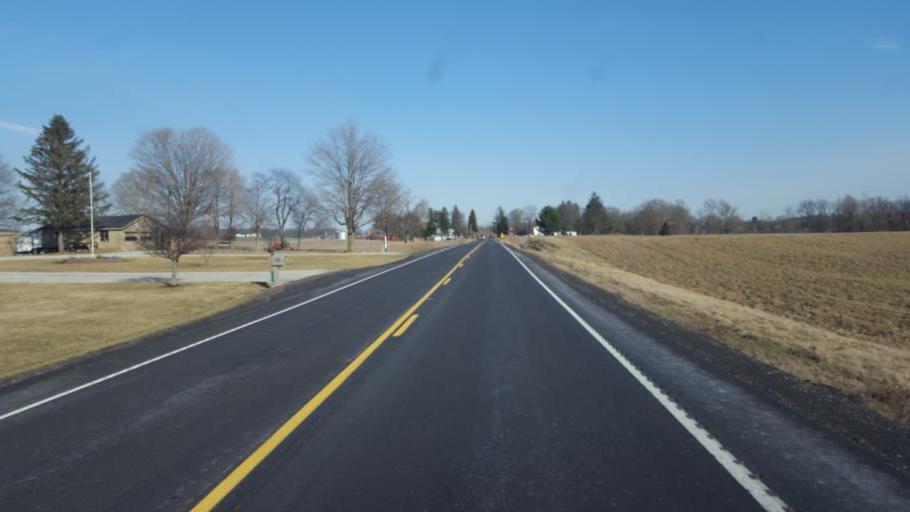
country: US
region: Ohio
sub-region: Knox County
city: Fredericktown
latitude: 40.4625
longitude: -82.6342
